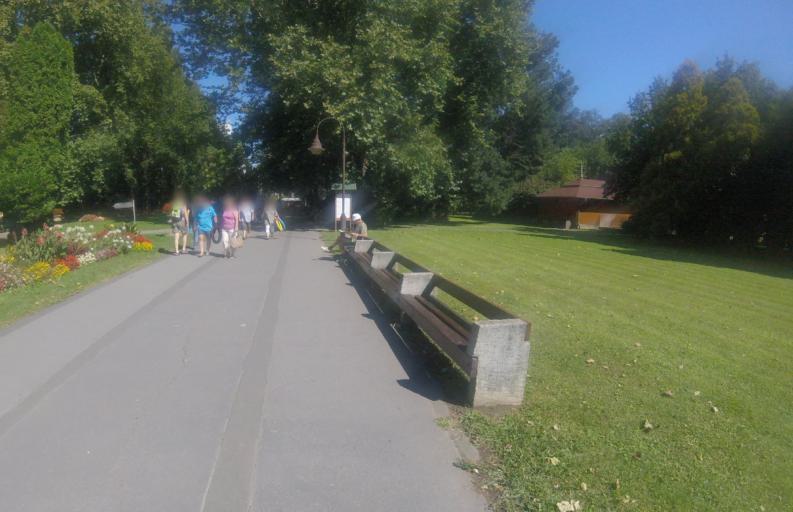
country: HU
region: Zala
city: Heviz
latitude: 46.7869
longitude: 17.1904
